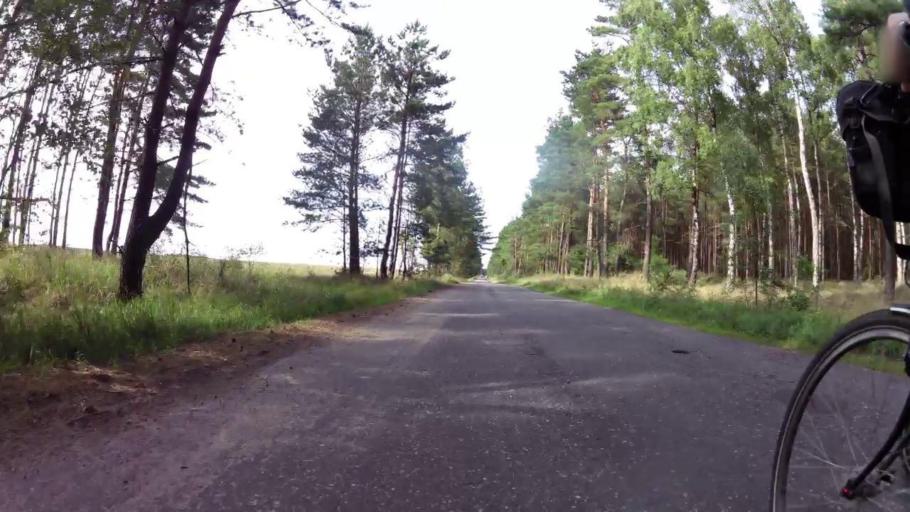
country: PL
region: West Pomeranian Voivodeship
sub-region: Powiat stargardzki
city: Insko
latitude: 53.3893
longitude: 15.5956
